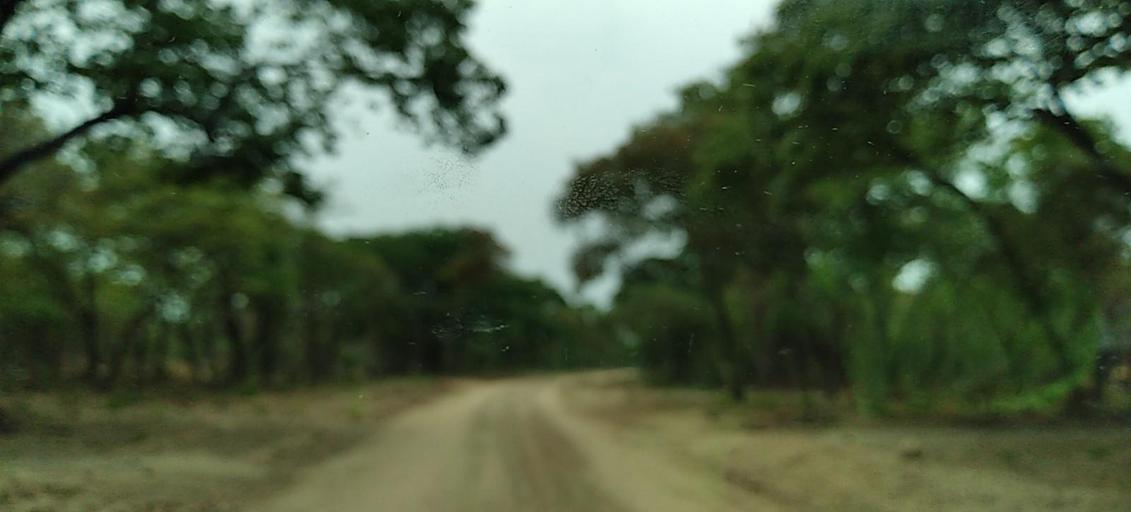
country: ZM
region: North-Western
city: Solwezi
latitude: -12.5412
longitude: 26.5260
